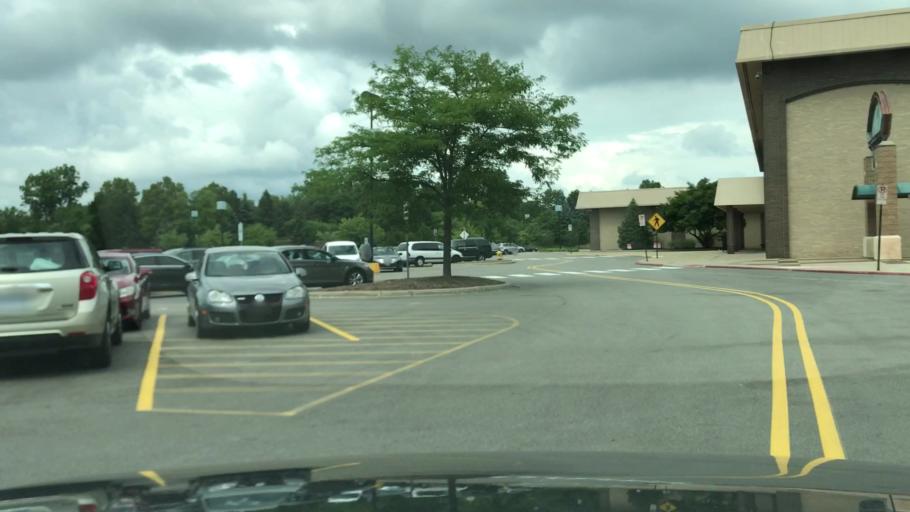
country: US
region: Michigan
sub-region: Kent County
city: East Grand Rapids
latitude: 42.9174
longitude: -85.5876
